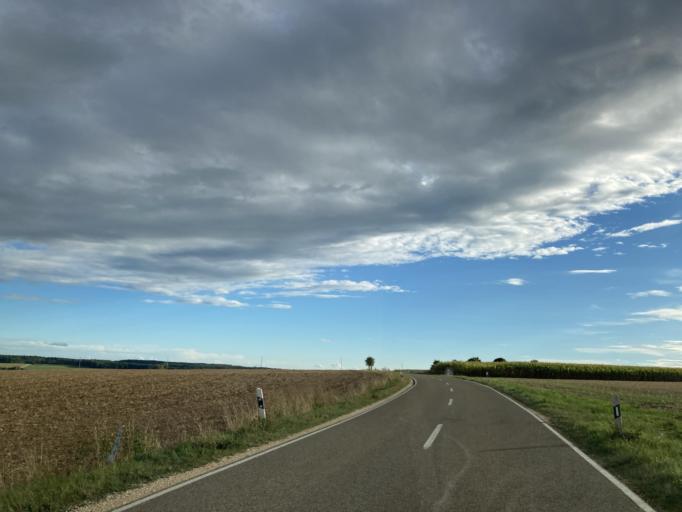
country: DE
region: Bavaria
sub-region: Swabia
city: Amerdingen
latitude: 48.7268
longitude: 10.4500
